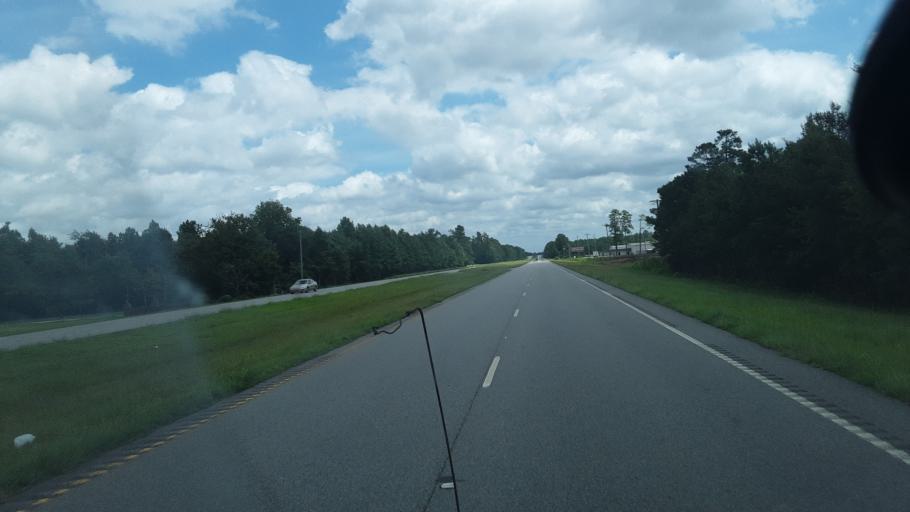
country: US
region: South Carolina
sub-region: Horry County
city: Loris
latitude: 34.0894
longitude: -78.8958
